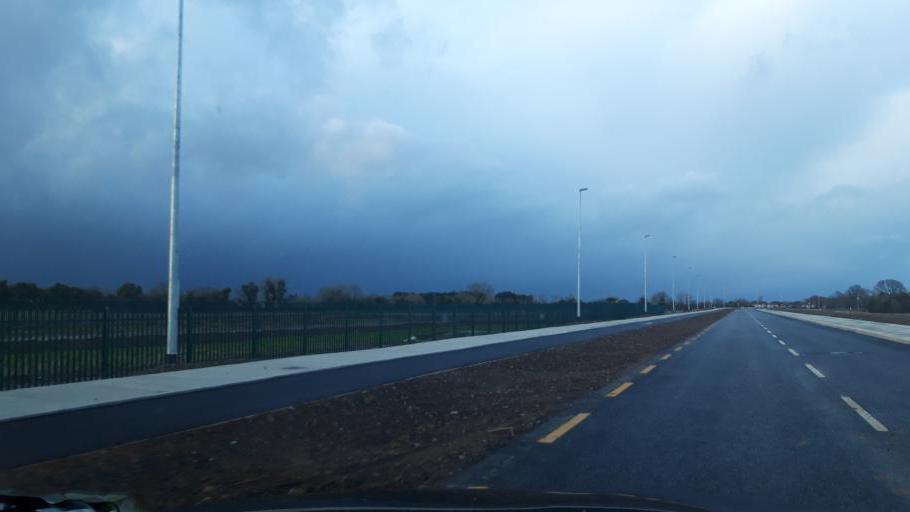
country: IE
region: Leinster
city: Donabate
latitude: 53.4846
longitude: -6.1376
